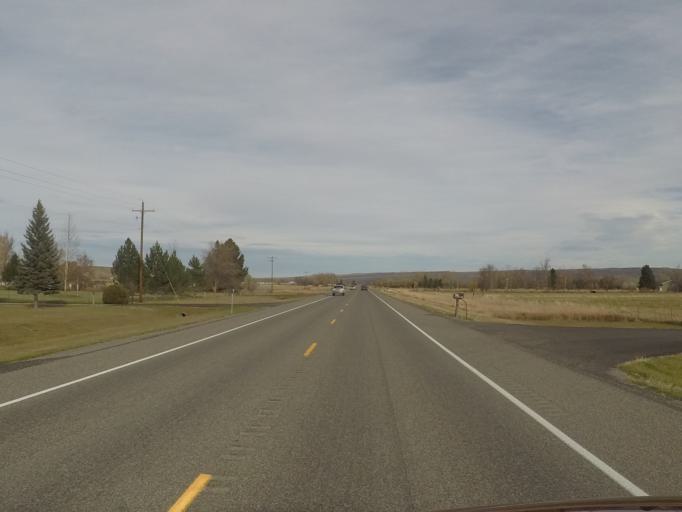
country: US
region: Montana
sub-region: Yellowstone County
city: Laurel
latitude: 45.5049
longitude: -108.9166
